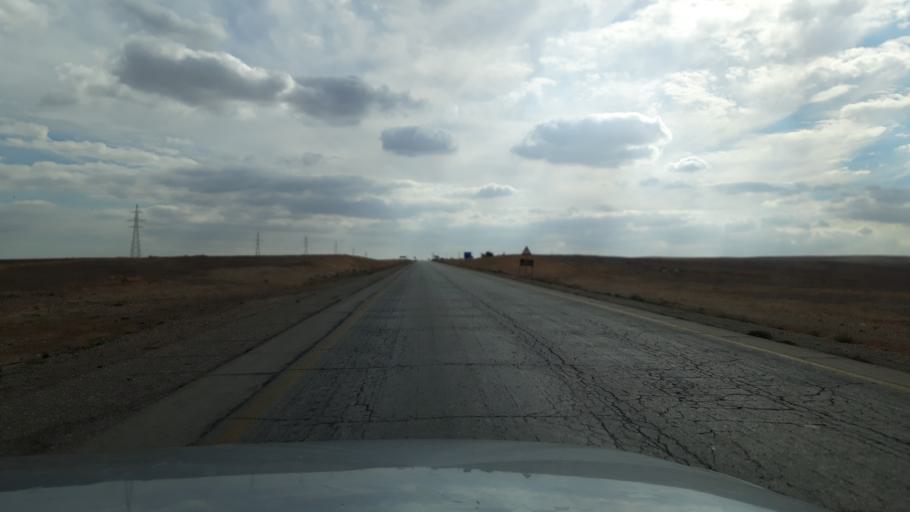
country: JO
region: Amman
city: Al Azraq ash Shamali
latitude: 31.7563
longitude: 36.5482
